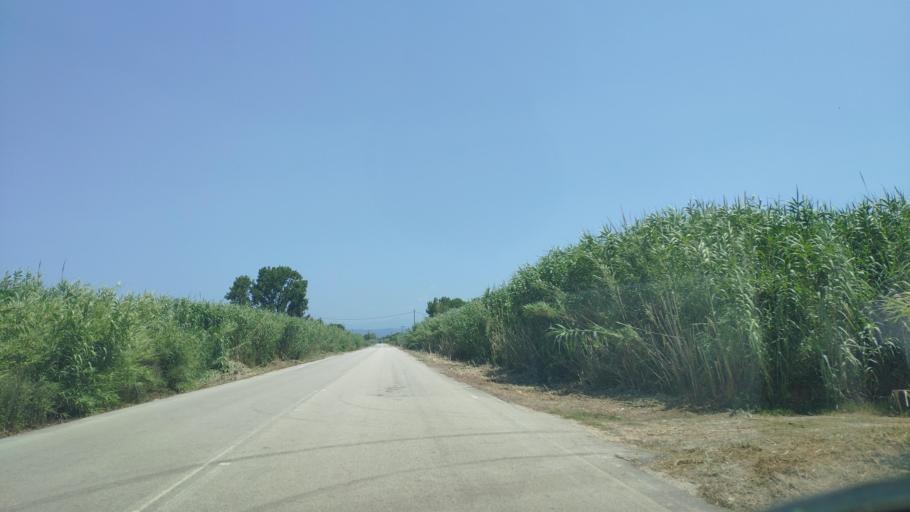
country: GR
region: Epirus
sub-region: Nomos Artas
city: Aneza
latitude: 39.0823
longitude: 20.8899
